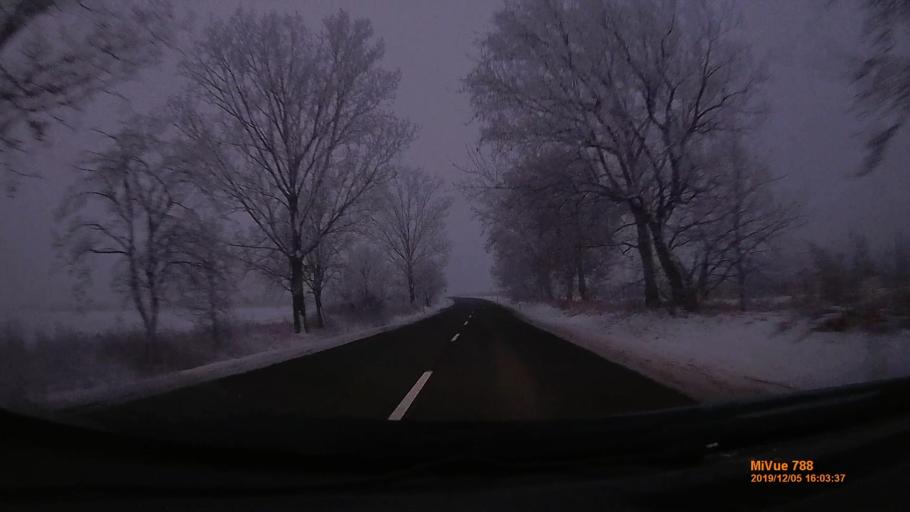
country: HU
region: Borsod-Abauj-Zemplen
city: Tarcal
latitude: 48.1041
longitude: 21.3658
